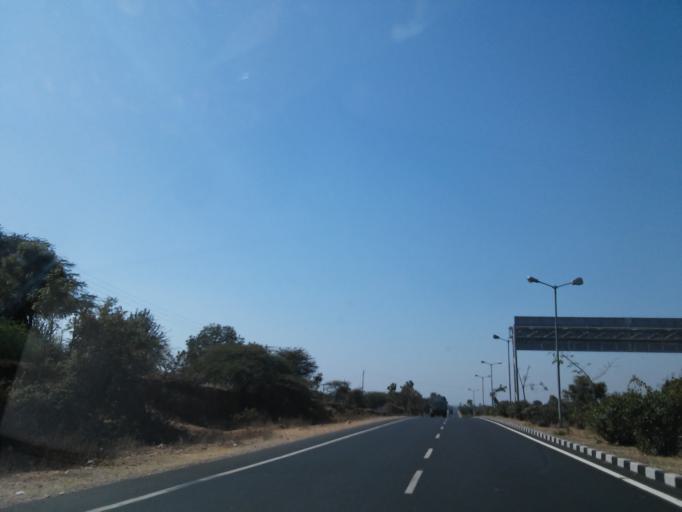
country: IN
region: Gujarat
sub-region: Sabar Kantha
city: Modasa
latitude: 23.6136
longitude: 73.2455
